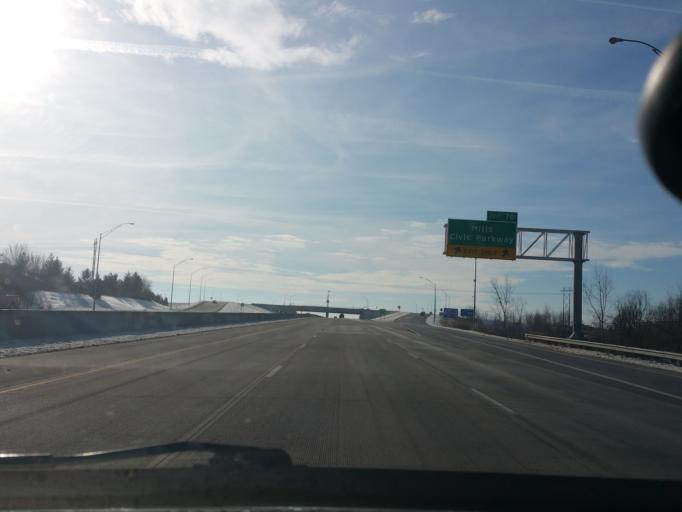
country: US
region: Iowa
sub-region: Polk County
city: Clive
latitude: 41.5644
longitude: -93.7771
